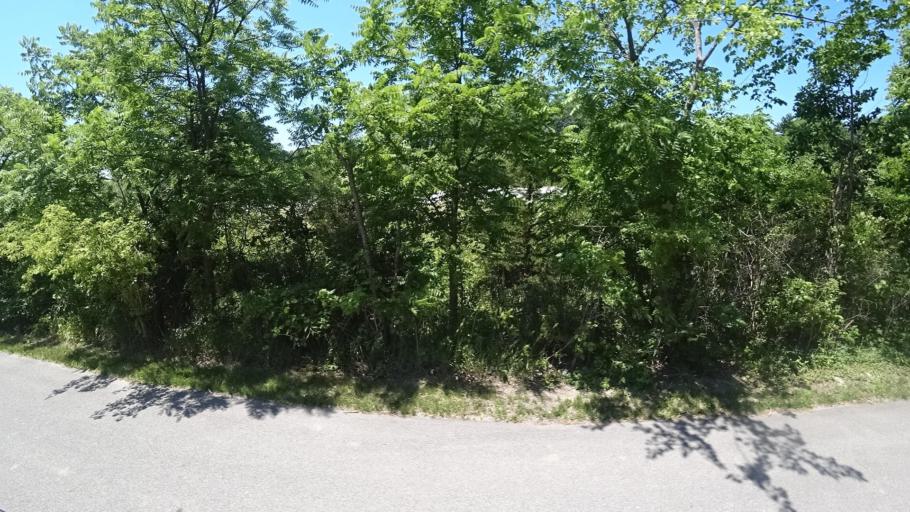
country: US
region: Indiana
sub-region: Porter County
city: Burns Harbor
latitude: 41.6041
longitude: -87.1247
